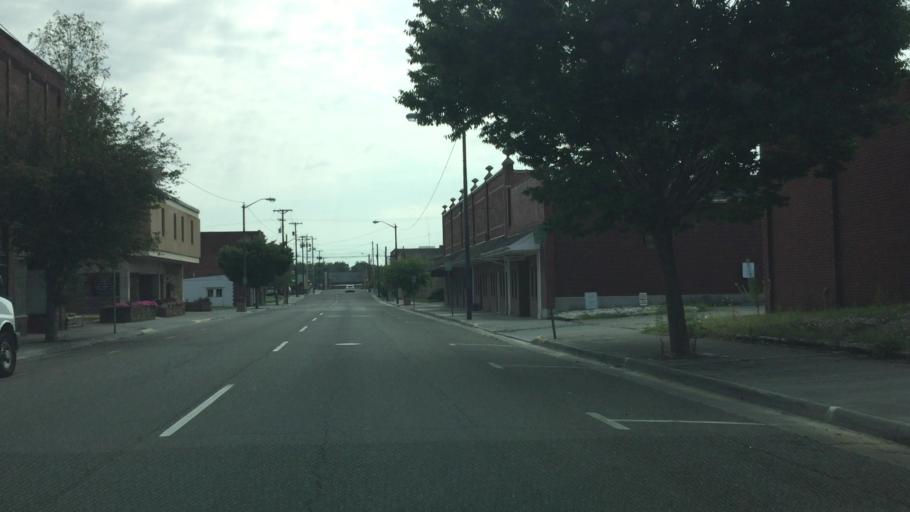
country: US
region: Virginia
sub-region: Pulaski County
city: Pulaski
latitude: 37.0477
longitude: -80.7789
